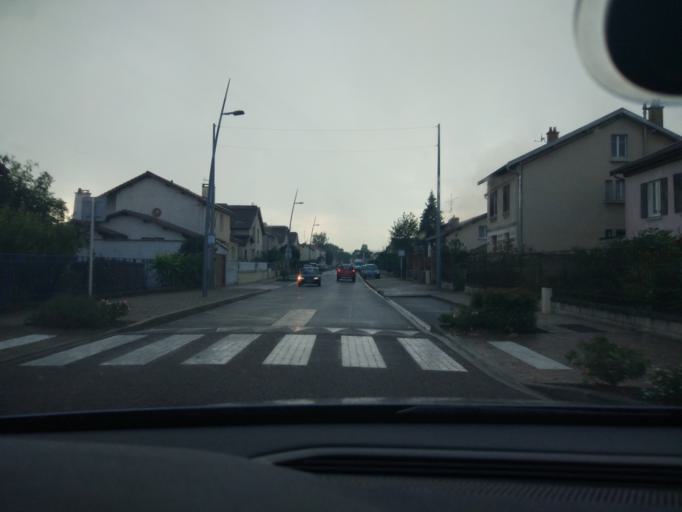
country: FR
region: Lorraine
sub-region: Departement de la Meuse
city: Verdun
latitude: 49.1730
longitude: 5.3876
